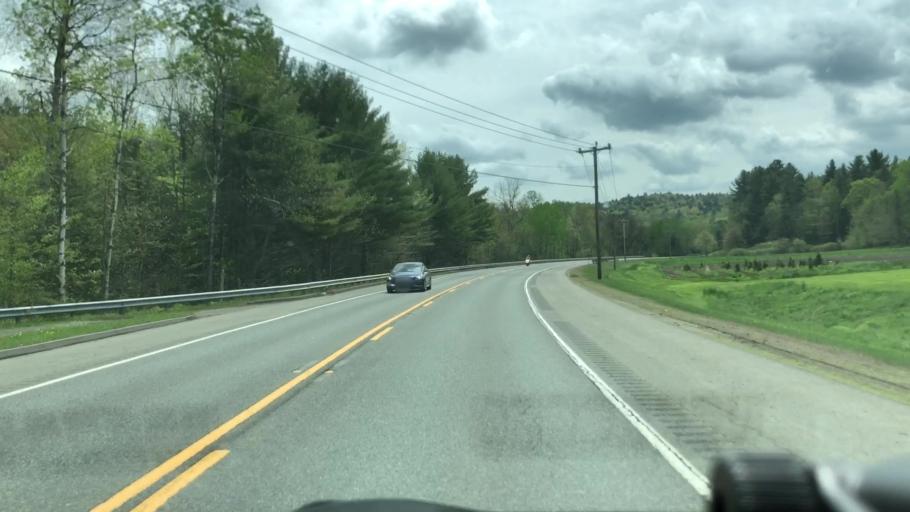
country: US
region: Massachusetts
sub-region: Hampshire County
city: Chesterfield
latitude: 42.4704
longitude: -72.9084
